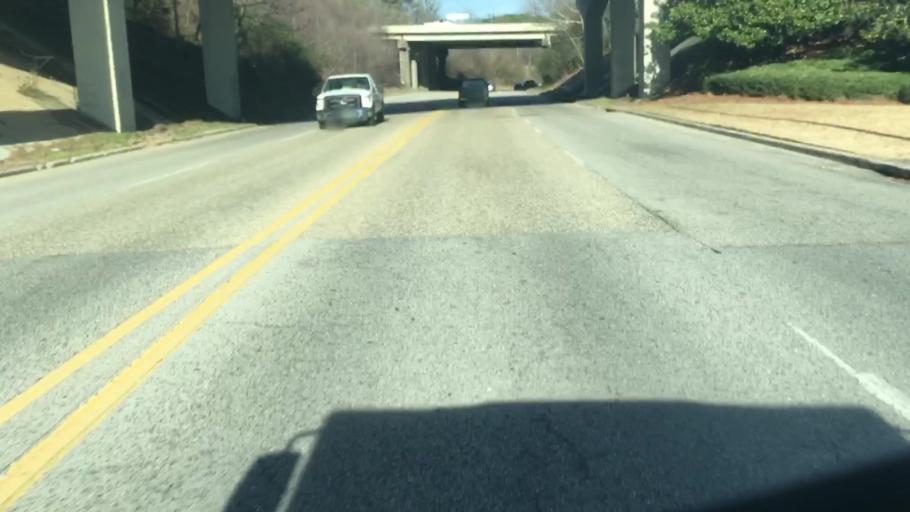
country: US
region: Alabama
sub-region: Jefferson County
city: Cahaba Heights
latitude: 33.4400
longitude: -86.7296
